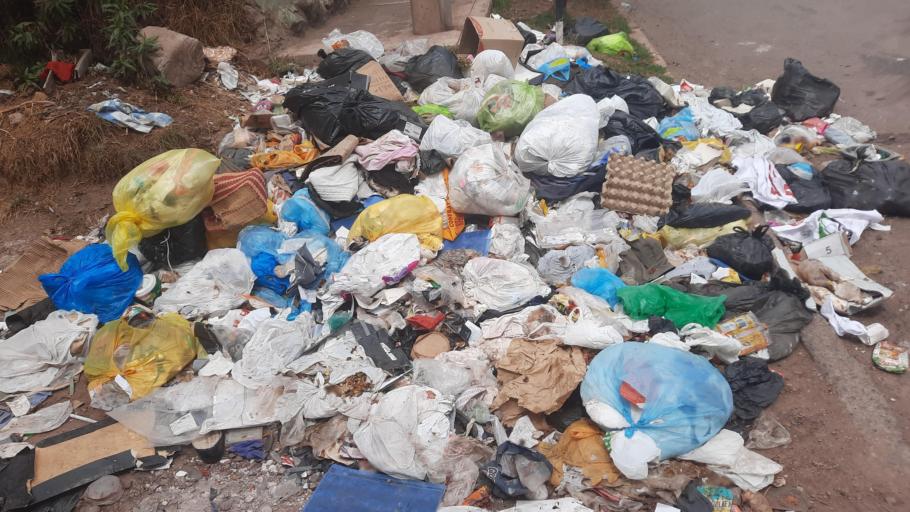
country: PE
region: Cusco
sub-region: Provincia de Cusco
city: Saylla
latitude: -13.5294
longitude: -71.9018
